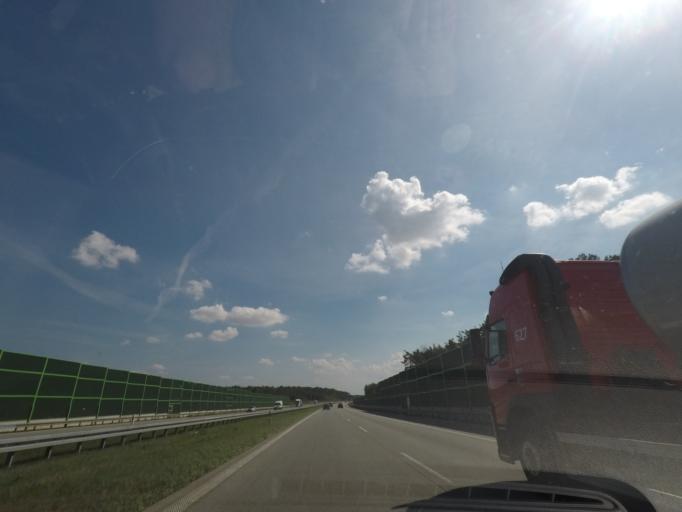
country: PL
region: Lodz Voivodeship
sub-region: Powiat lodzki wschodni
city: Andrespol
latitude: 51.7230
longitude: 19.6073
